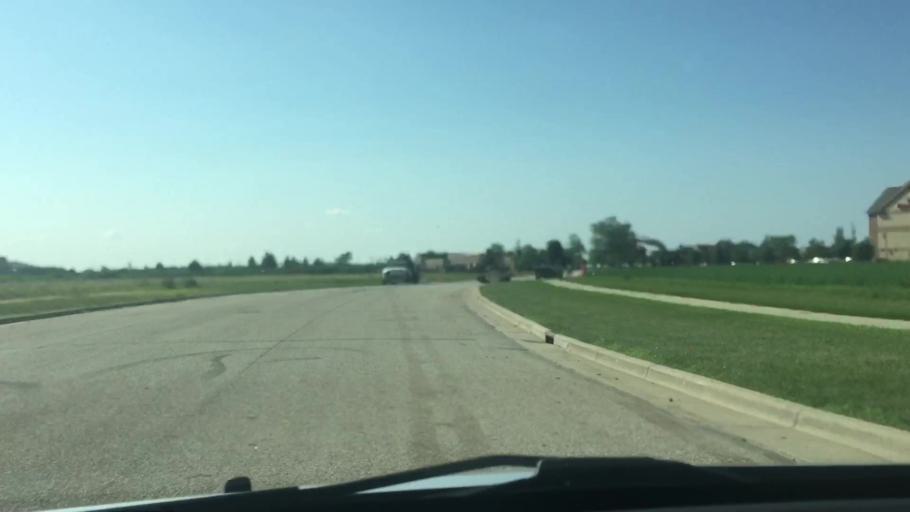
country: US
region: Wisconsin
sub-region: Waukesha County
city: Oconomowoc
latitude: 43.0722
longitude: -88.4652
